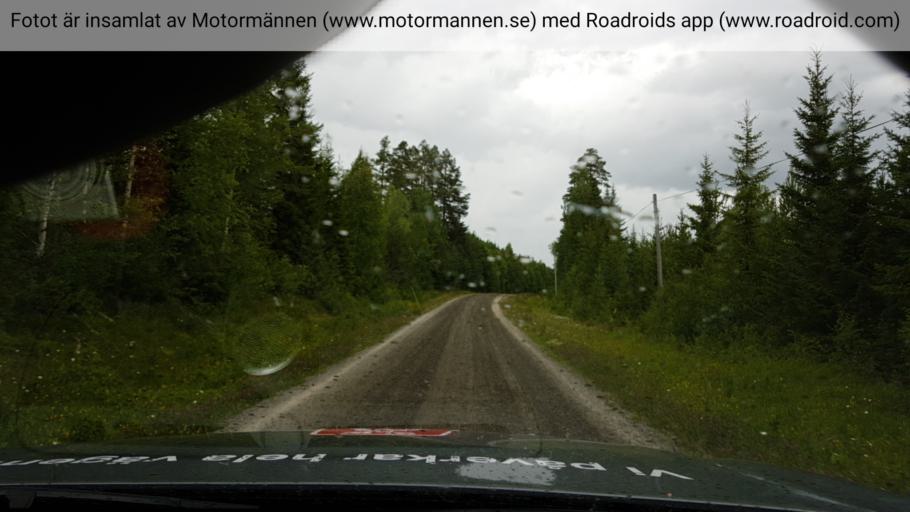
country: SE
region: Jaemtland
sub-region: Bergs Kommun
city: Hoverberg
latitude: 62.5194
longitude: 14.7076
